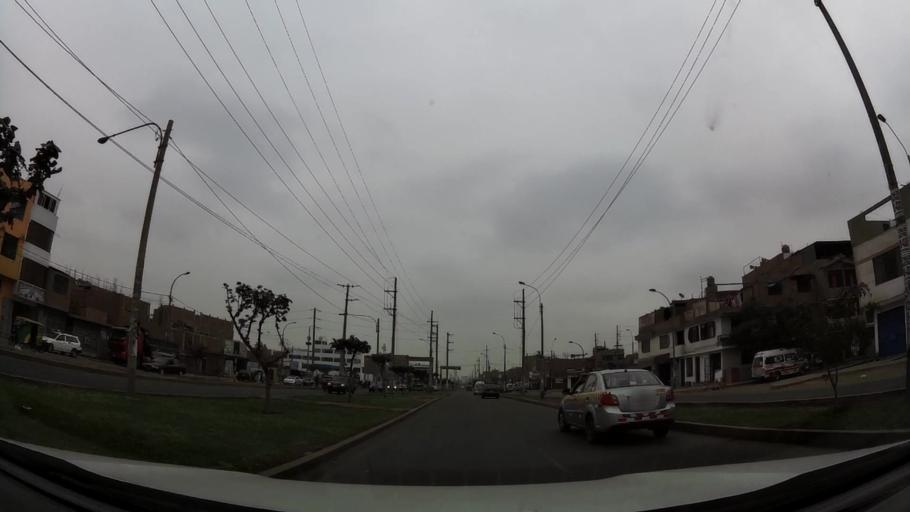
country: PE
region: Lima
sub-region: Lima
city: Independencia
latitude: -11.9473
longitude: -77.0762
